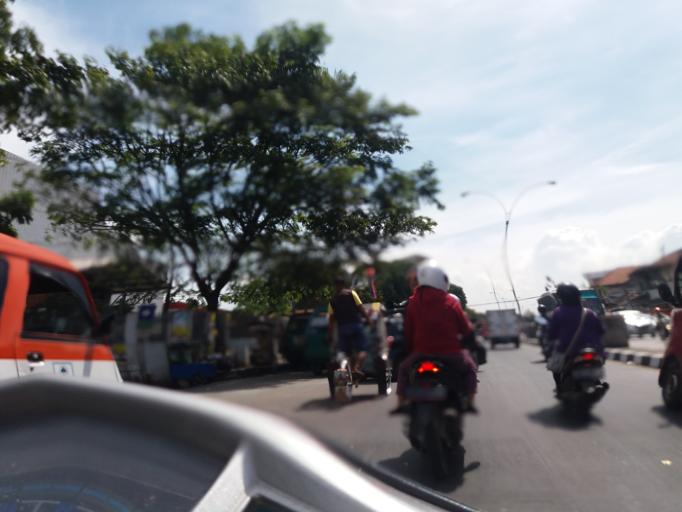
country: ID
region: West Java
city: Margahayukencana
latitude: -6.9416
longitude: 107.5827
